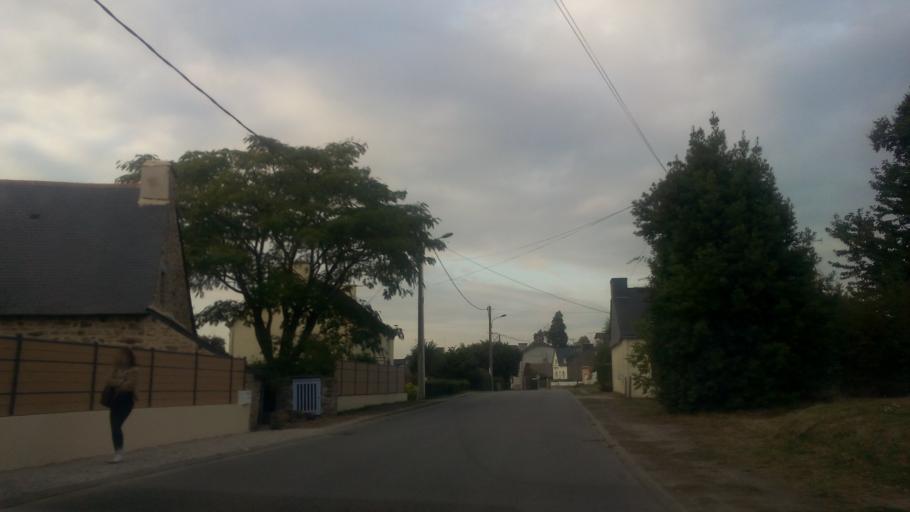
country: FR
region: Brittany
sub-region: Departement du Morbihan
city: Peillac
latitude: 47.7108
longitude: -2.2154
